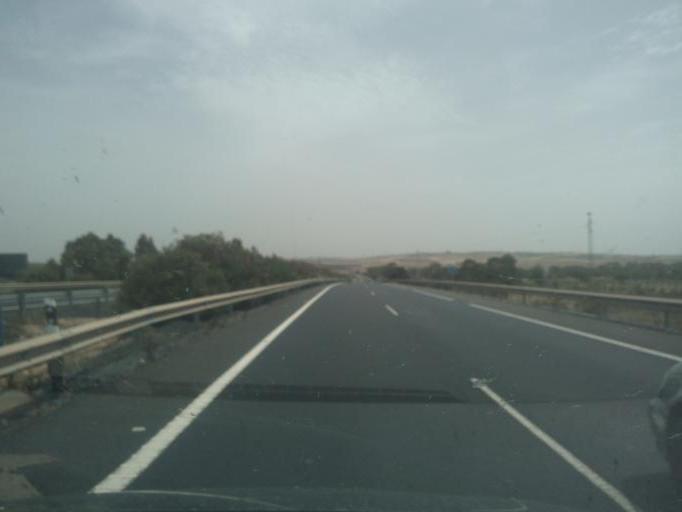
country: ES
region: Andalusia
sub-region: Provincia de Huelva
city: Lucena del Puerto
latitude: 37.3408
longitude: -6.7206
